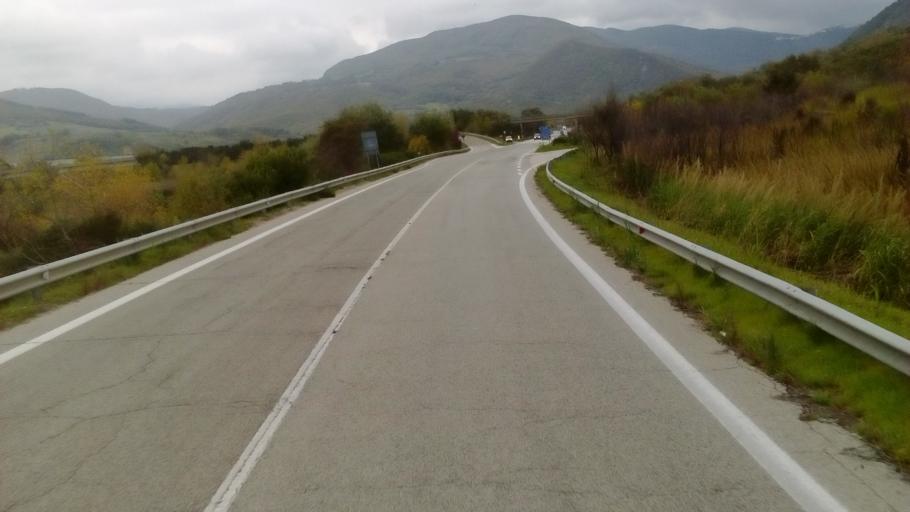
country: IT
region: Abruzzo
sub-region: Provincia di Chieti
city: Dogliola
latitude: 41.9326
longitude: 14.6645
